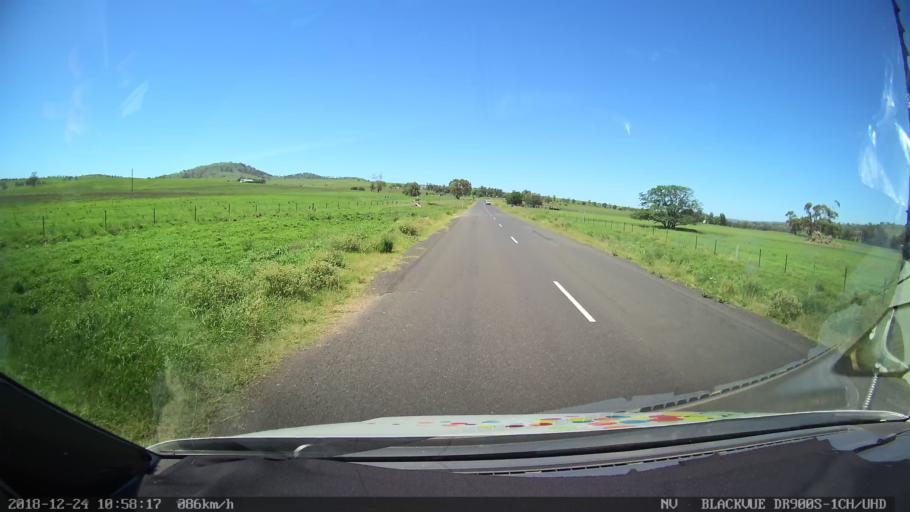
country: AU
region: New South Wales
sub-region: Upper Hunter Shire
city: Merriwa
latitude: -32.0455
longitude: 150.4069
